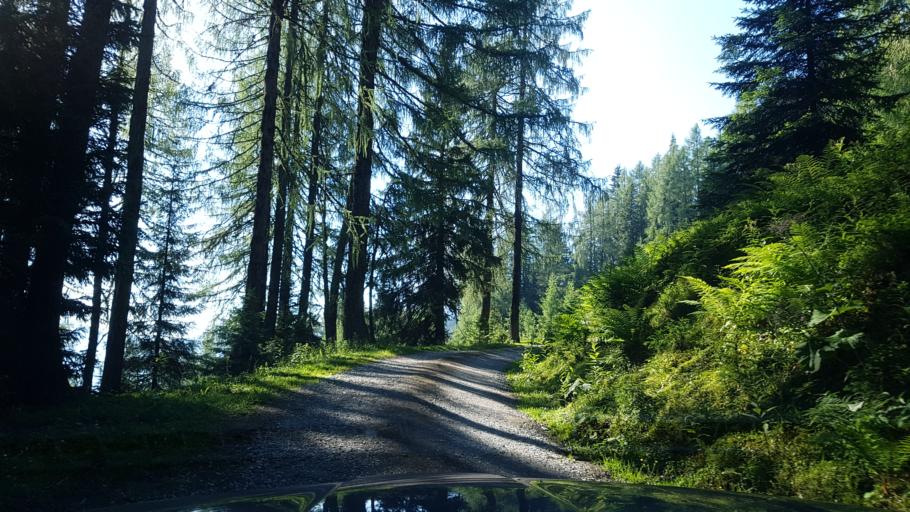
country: AT
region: Salzburg
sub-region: Politischer Bezirk Sankt Johann im Pongau
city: Dorfgastein
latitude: 47.2419
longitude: 13.0698
